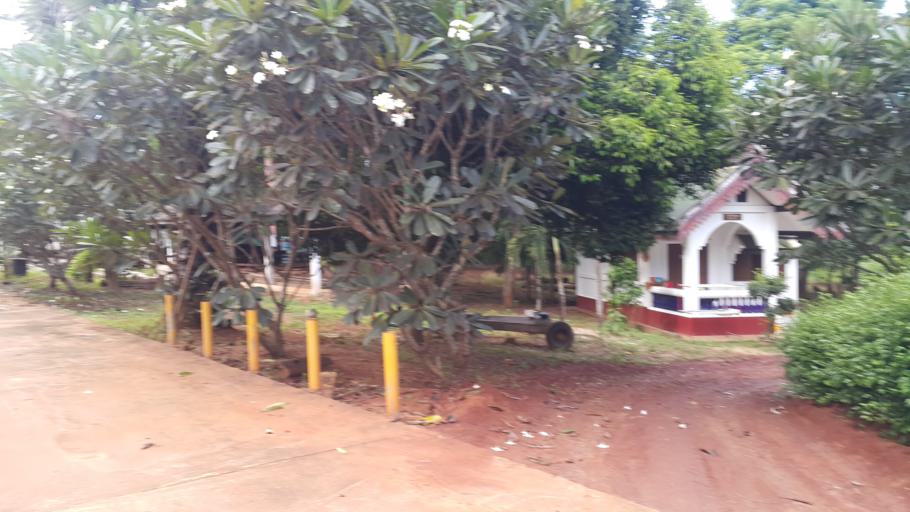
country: TH
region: Chiang Mai
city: Mae Taeng
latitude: 19.1579
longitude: 98.9764
